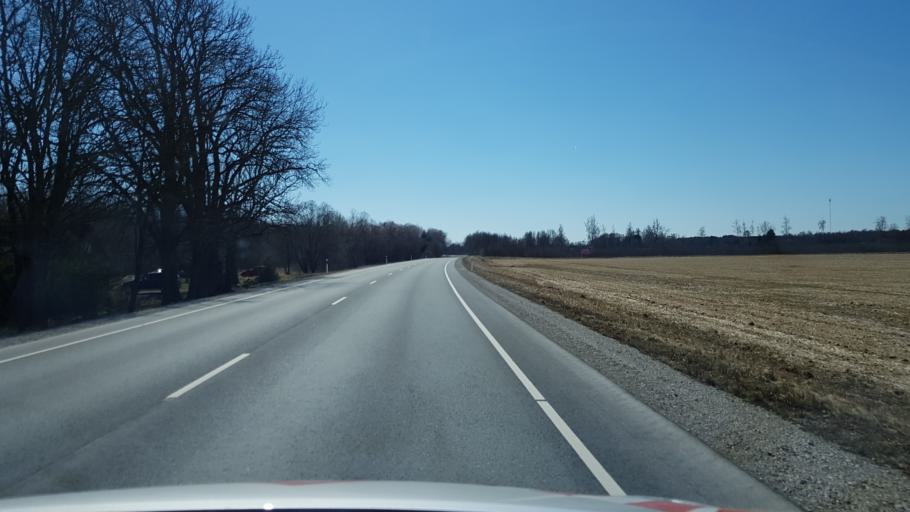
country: EE
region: Laeaene
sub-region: Lihula vald
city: Lihula
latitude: 58.8483
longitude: 24.0663
